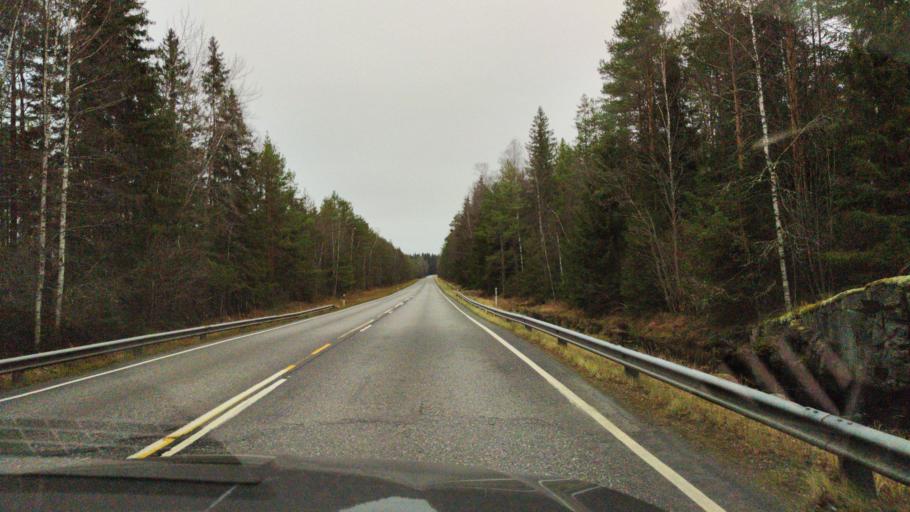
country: FI
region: Varsinais-Suomi
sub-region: Loimaa
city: Ylaene
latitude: 60.7458
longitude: 22.4265
